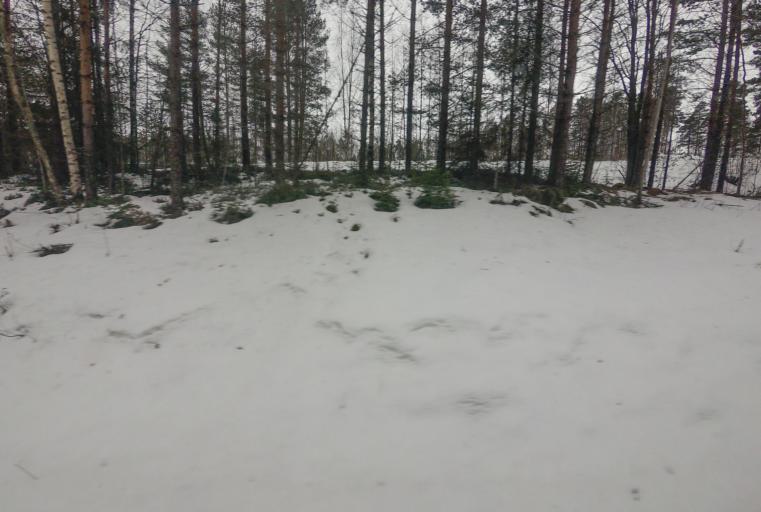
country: FI
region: Southern Savonia
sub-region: Savonlinna
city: Savonlinna
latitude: 61.8584
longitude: 28.9530
